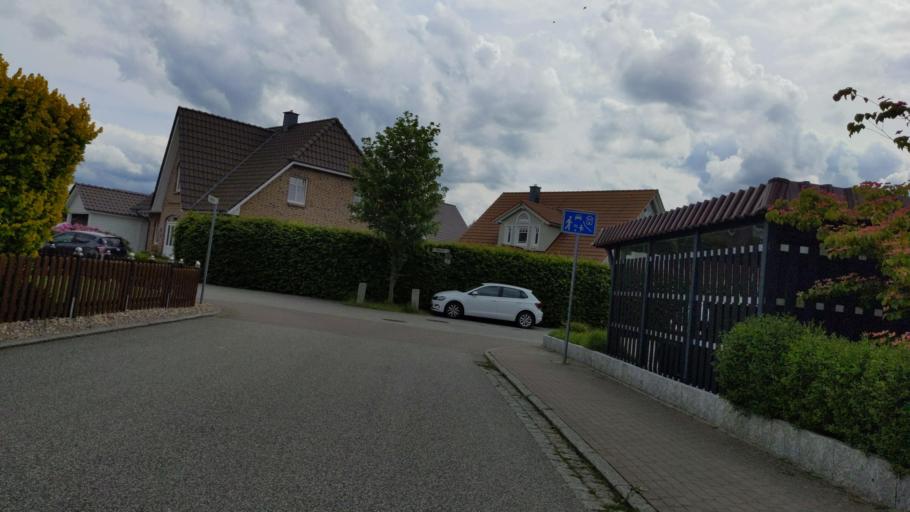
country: DE
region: Schleswig-Holstein
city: Luebeck
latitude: 53.8233
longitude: 10.6831
